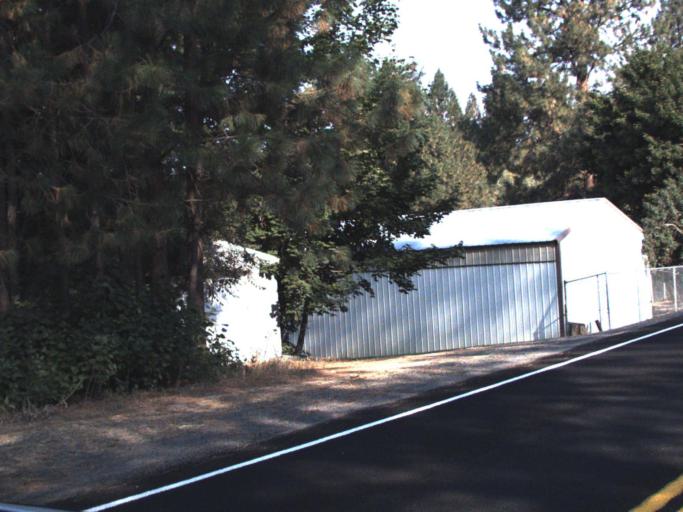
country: US
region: Washington
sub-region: Spokane County
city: Deer Park
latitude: 47.8904
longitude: -117.6601
